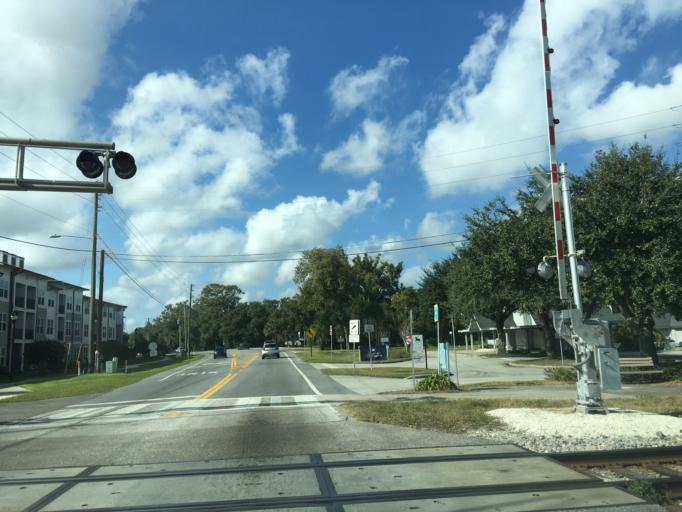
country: US
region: Florida
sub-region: Orange County
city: Maitland
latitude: 28.6186
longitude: -81.3673
